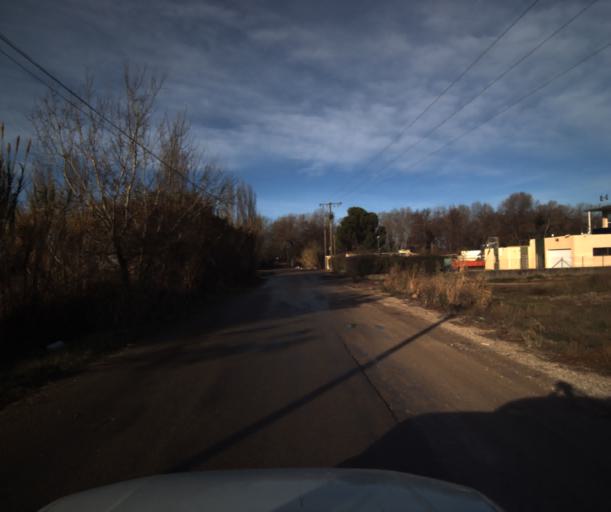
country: FR
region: Provence-Alpes-Cote d'Azur
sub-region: Departement du Vaucluse
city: Pertuis
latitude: 43.6758
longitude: 5.4821
